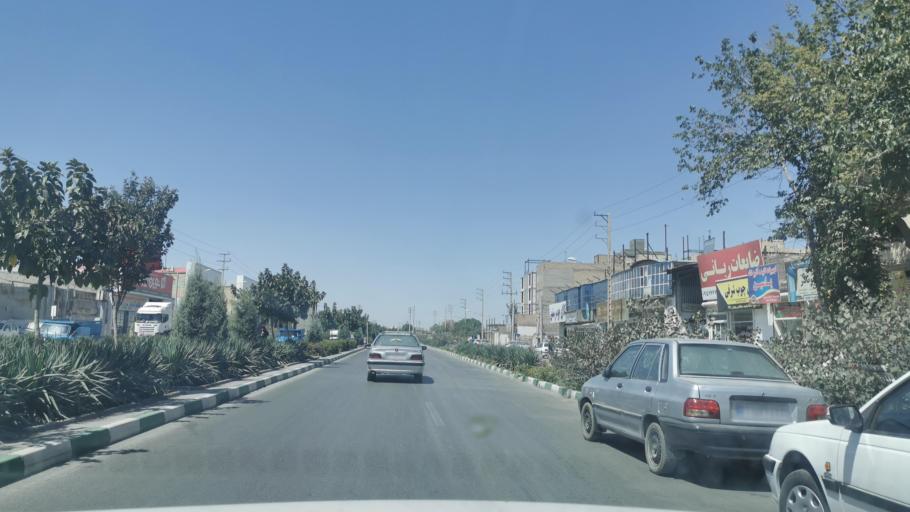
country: IR
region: Razavi Khorasan
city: Mashhad
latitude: 36.3512
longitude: 59.5747
